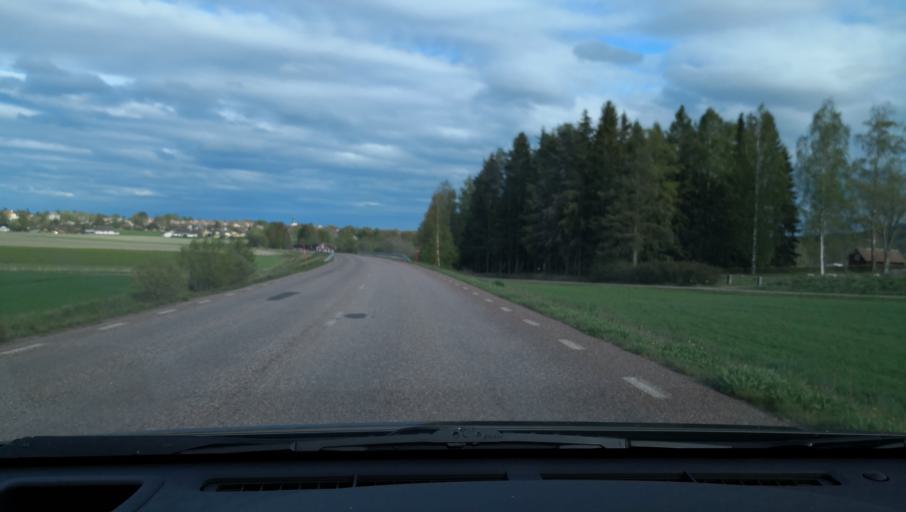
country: SE
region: Dalarna
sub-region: Hedemora Kommun
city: Hedemora
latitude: 60.2828
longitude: 15.9500
